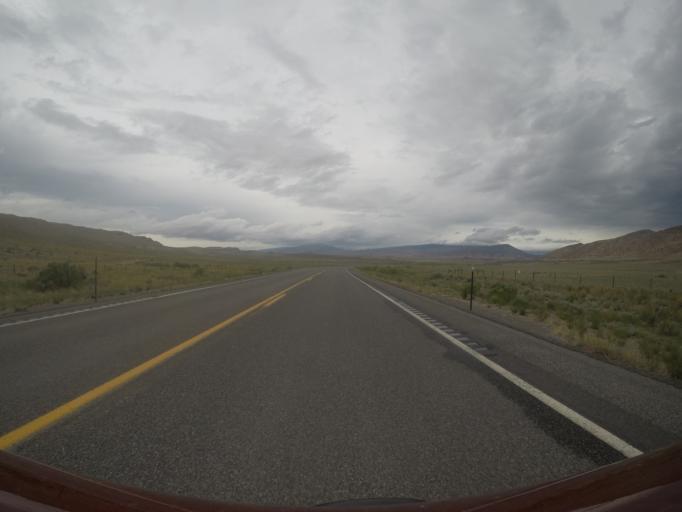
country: US
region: Wyoming
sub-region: Big Horn County
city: Lovell
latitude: 44.9237
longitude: -108.2984
